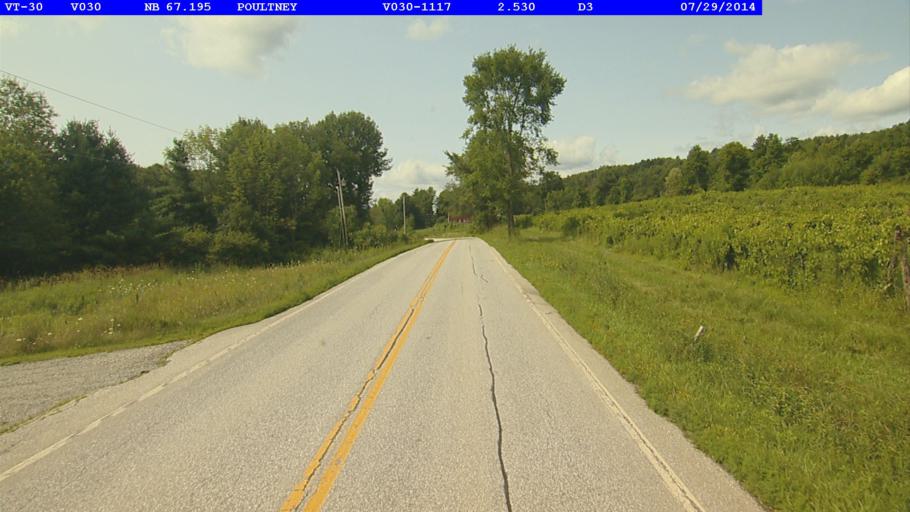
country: US
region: Vermont
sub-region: Rutland County
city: Poultney
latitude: 43.4985
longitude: -73.2072
